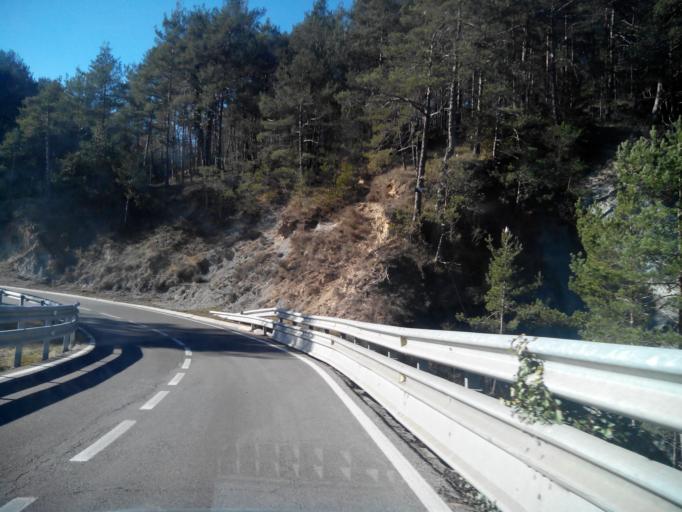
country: ES
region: Catalonia
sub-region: Provincia de Barcelona
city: Vilada
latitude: 42.1338
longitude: 1.9175
